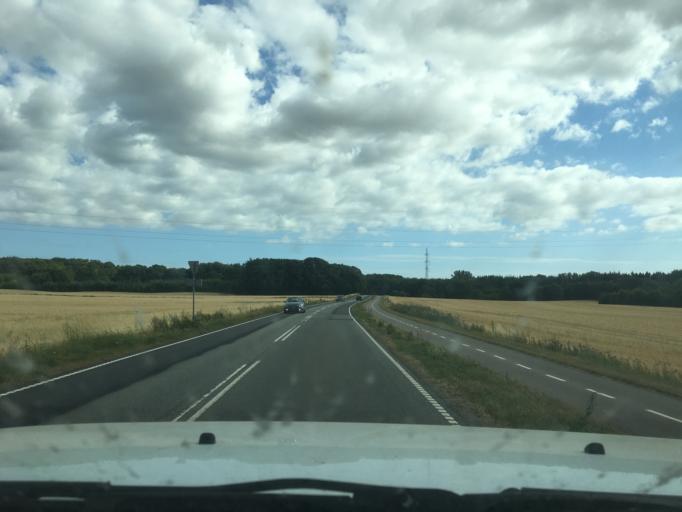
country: DK
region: Central Jutland
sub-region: Syddjurs Kommune
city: Hornslet
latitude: 56.3032
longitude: 10.3169
